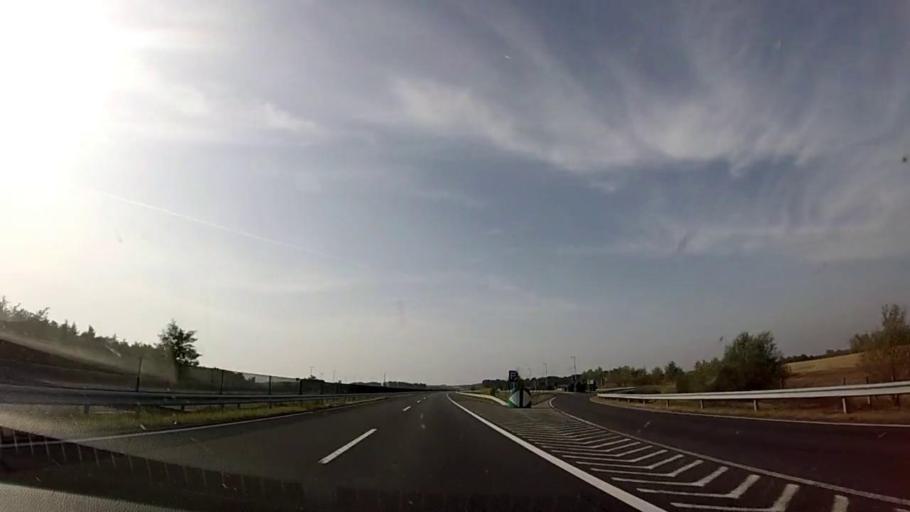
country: HU
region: Somogy
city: Balatonbereny
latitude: 46.6286
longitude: 17.2768
